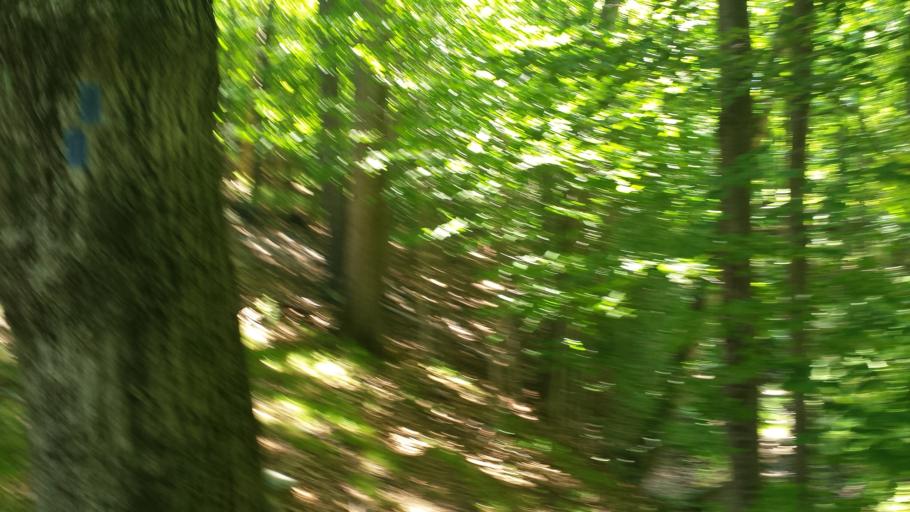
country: US
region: New York
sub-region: Westchester County
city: Mount Kisco
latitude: 41.1778
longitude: -73.7057
